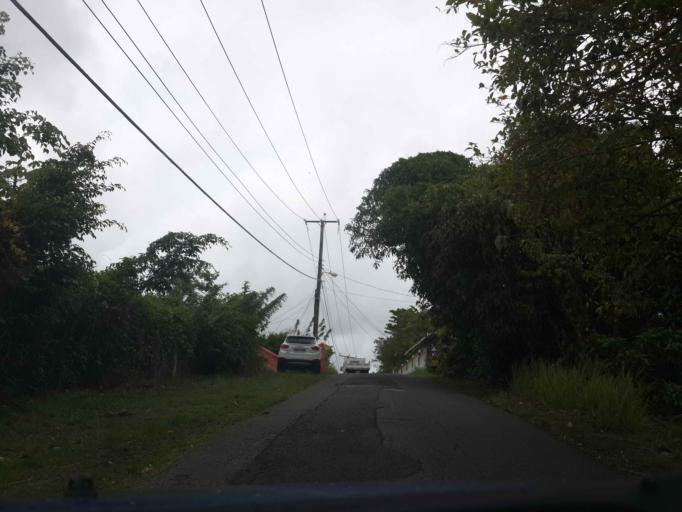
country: LC
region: Castries Quarter
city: Castries
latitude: 13.9946
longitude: -60.9797
